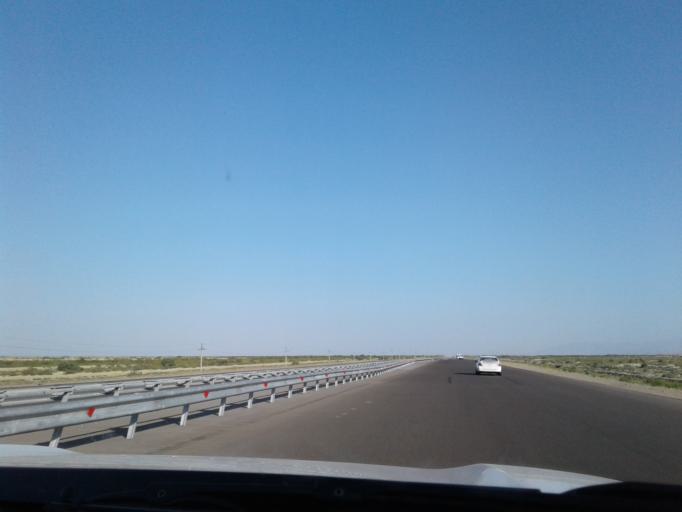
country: TM
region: Balkan
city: Serdar
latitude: 38.8916
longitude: 56.5297
